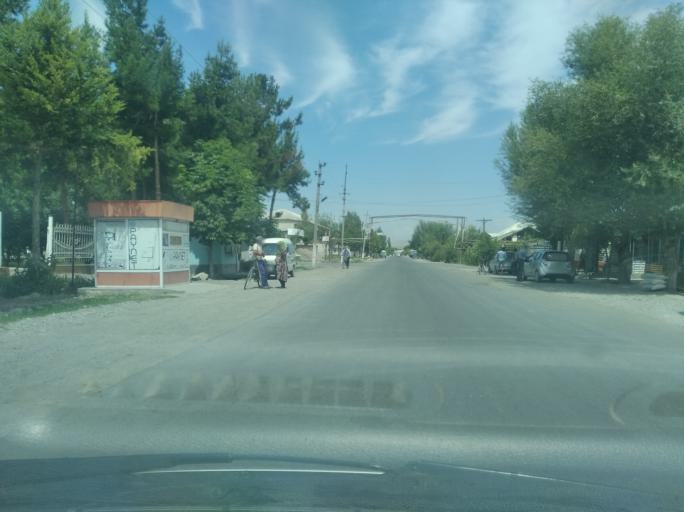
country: KG
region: Osh
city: Aravan
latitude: 40.6125
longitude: 72.4562
